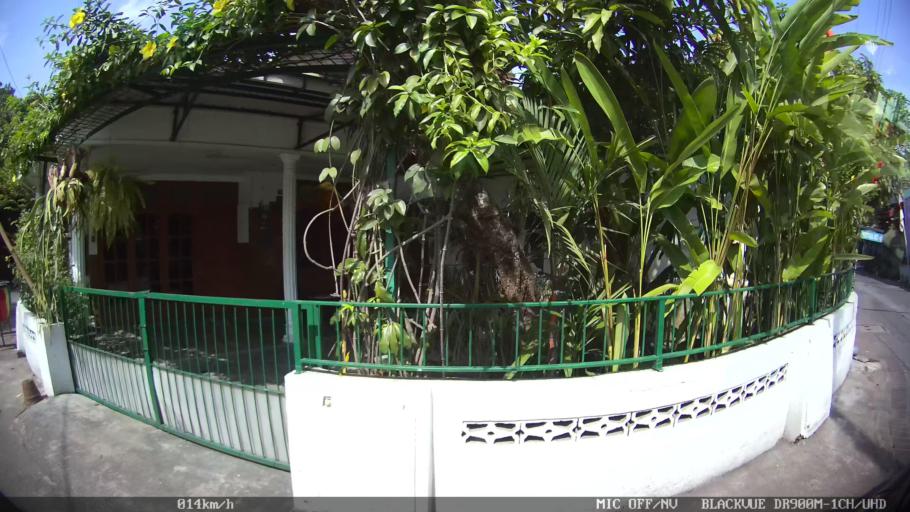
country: ID
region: Daerah Istimewa Yogyakarta
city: Kasihan
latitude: -7.8286
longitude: 110.3706
